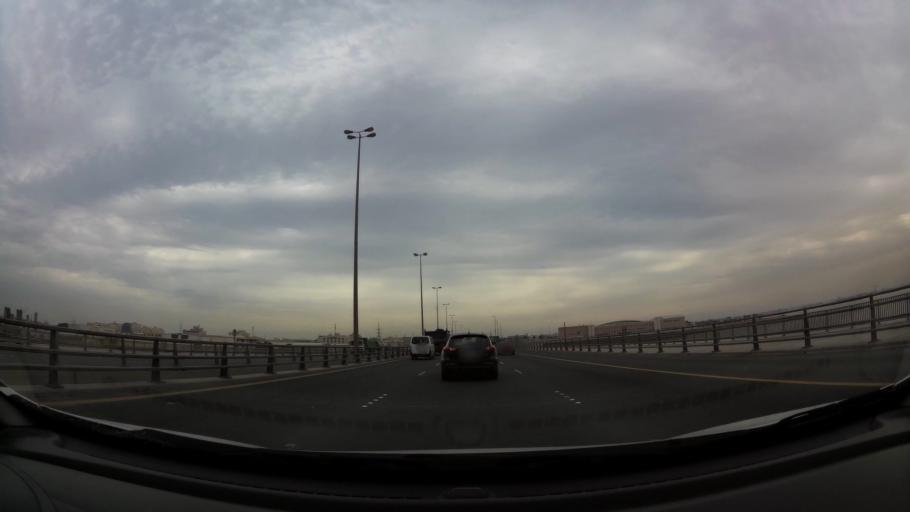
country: BH
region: Northern
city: Sitrah
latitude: 26.1748
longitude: 50.5972
